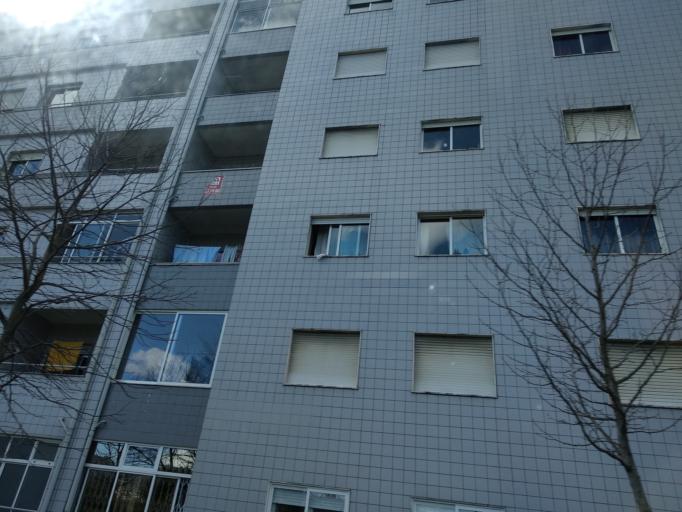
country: PT
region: Braga
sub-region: Braga
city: Braga
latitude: 41.5594
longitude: -8.4034
